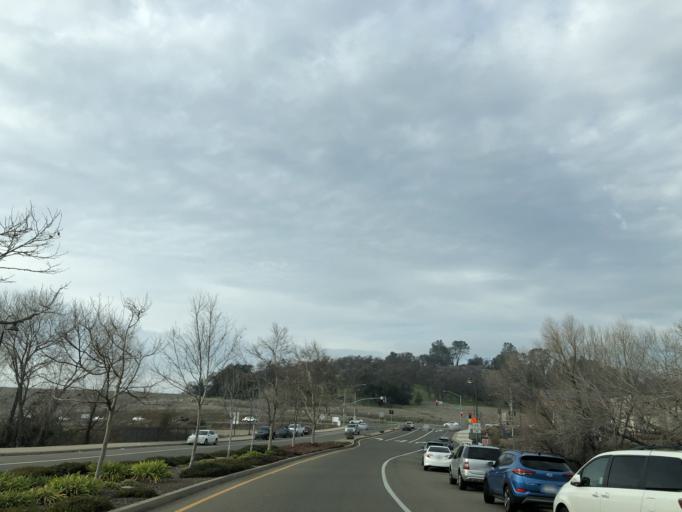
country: US
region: California
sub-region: El Dorado County
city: El Dorado Hills
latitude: 38.6999
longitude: -121.1059
